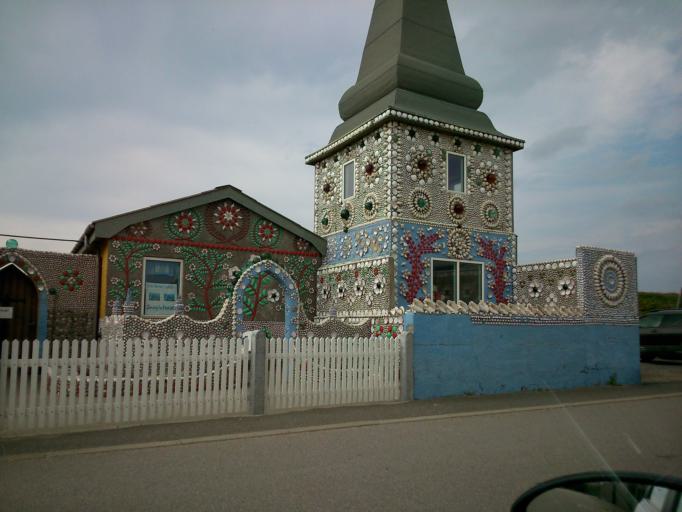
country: DK
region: Central Jutland
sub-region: Lemvig Kommune
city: Thyboron
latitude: 56.6963
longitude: 8.2009
